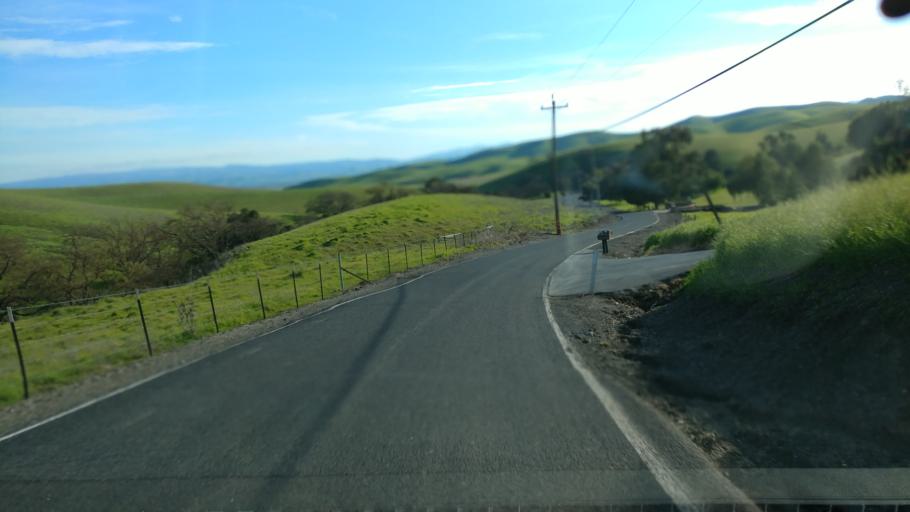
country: US
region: California
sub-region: Alameda County
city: Livermore
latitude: 37.7717
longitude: -121.7798
